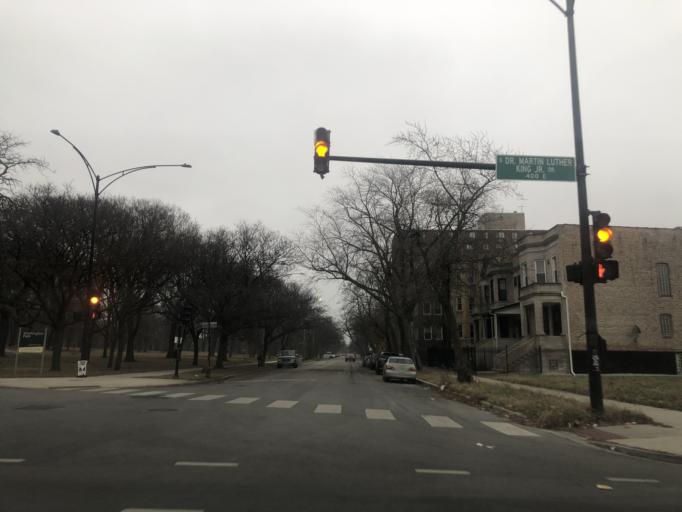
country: US
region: Illinois
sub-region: Cook County
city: Chicago
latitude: 41.7857
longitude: -87.6158
